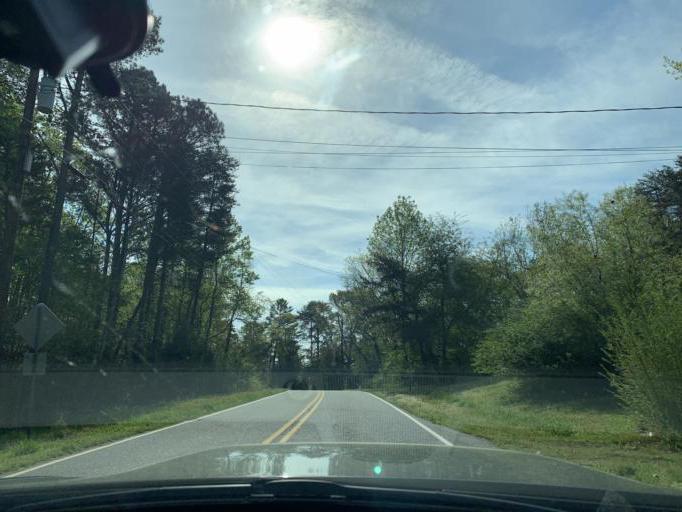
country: US
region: Georgia
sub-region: Forsyth County
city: Cumming
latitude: 34.2481
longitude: -84.1183
